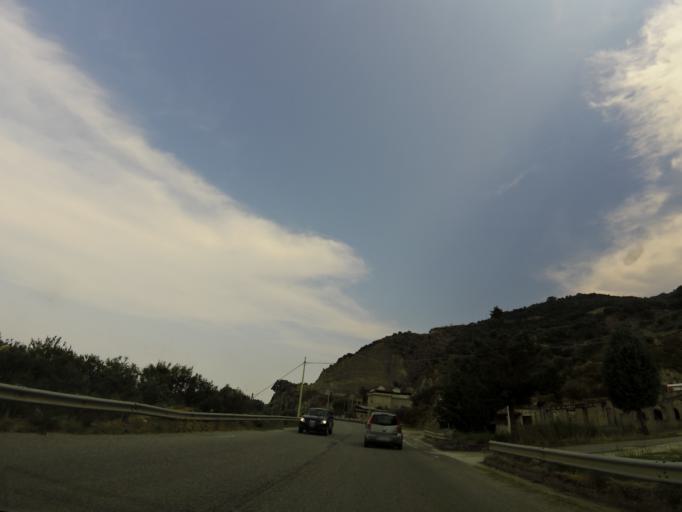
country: IT
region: Calabria
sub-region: Provincia di Reggio Calabria
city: Stilo
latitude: 38.4659
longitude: 16.4870
